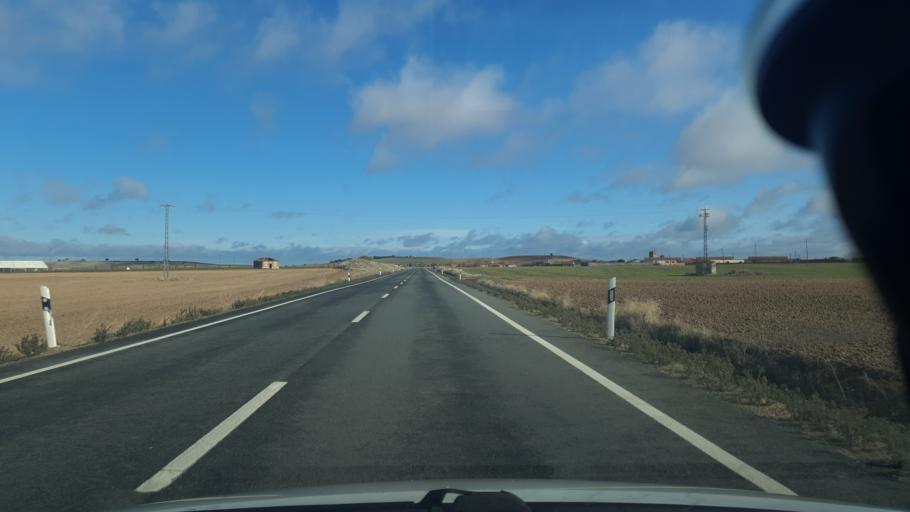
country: ES
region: Castille and Leon
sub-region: Provincia de Segovia
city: Codorniz
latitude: 41.0623
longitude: -4.6107
